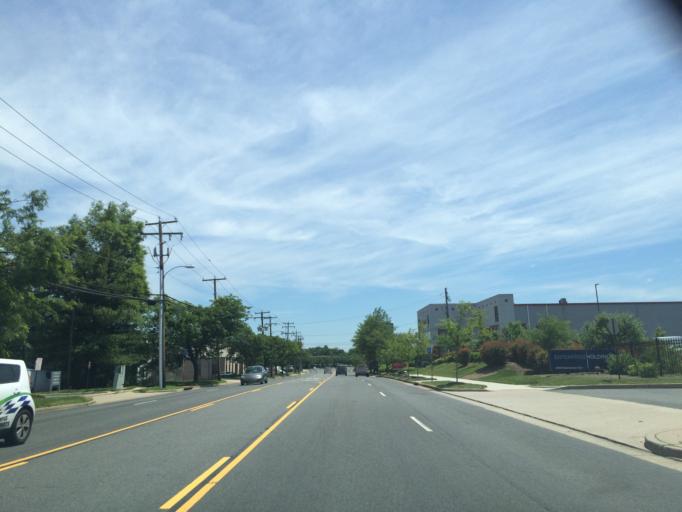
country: US
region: Virginia
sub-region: Fairfax County
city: Rose Hill
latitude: 38.8036
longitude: -77.1167
